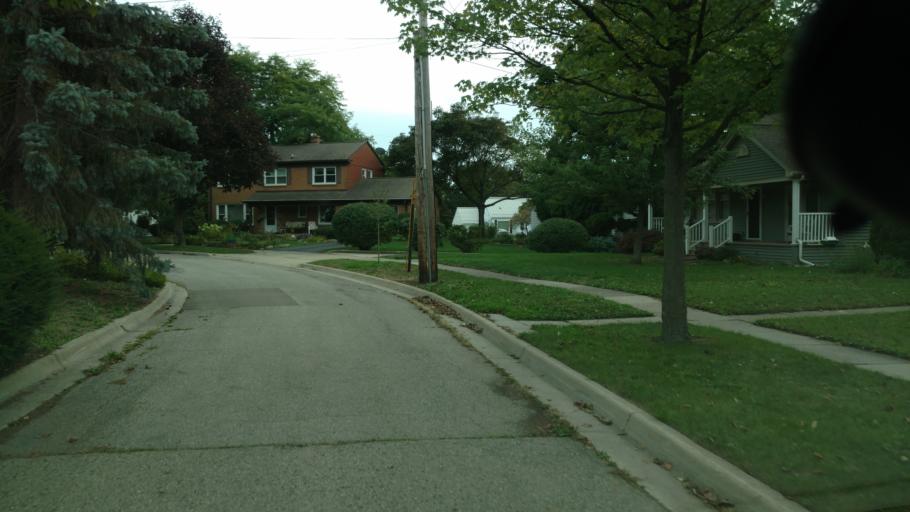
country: US
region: Michigan
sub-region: Ingham County
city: East Lansing
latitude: 42.7383
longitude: -84.5139
